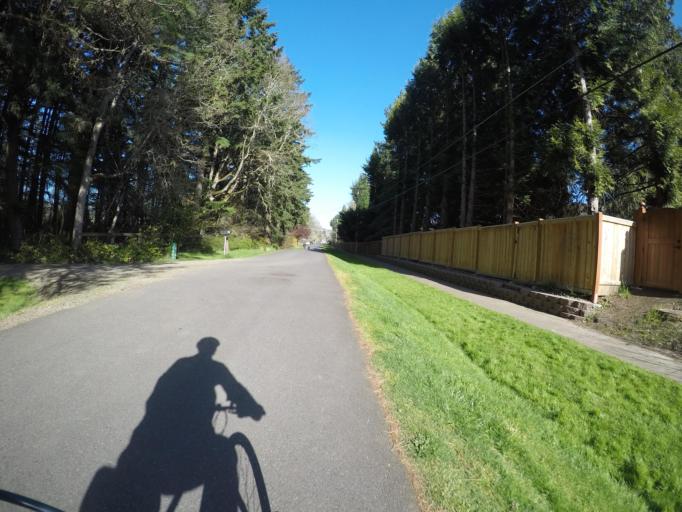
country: US
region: Oregon
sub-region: Washington County
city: Oak Hills
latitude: 45.5470
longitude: -122.8218
